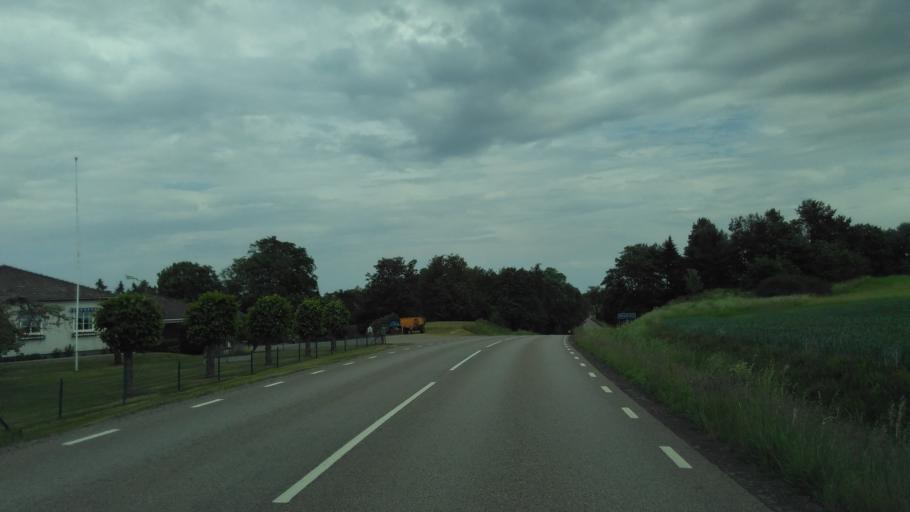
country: SE
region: Vaestra Goetaland
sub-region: Vara Kommun
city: Kvanum
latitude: 58.3980
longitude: 13.1585
